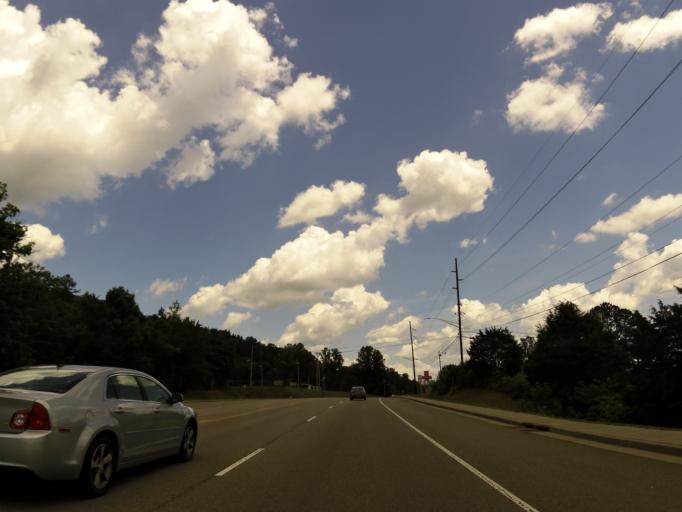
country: US
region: Tennessee
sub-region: Union County
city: Maynardville
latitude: 36.2462
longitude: -83.8089
